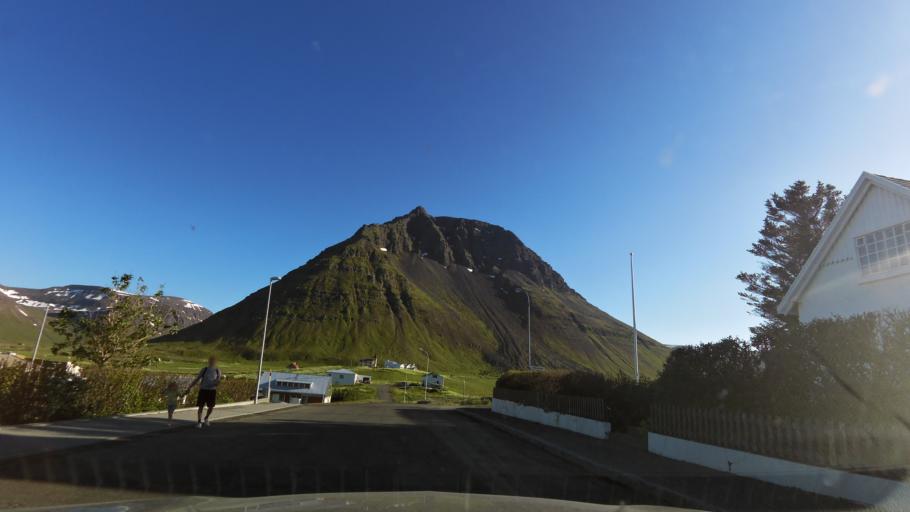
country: IS
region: Westfjords
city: Isafjoerdur
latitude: 66.1572
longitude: -23.2563
